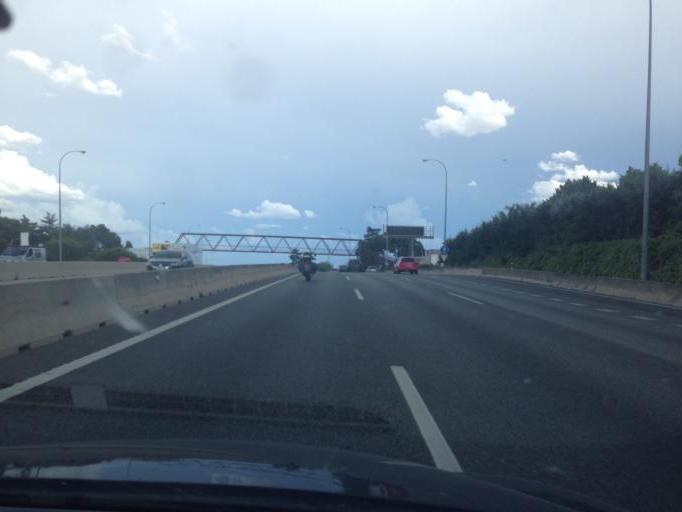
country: ES
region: Madrid
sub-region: Provincia de Madrid
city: Majadahonda
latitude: 40.4762
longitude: -3.8400
